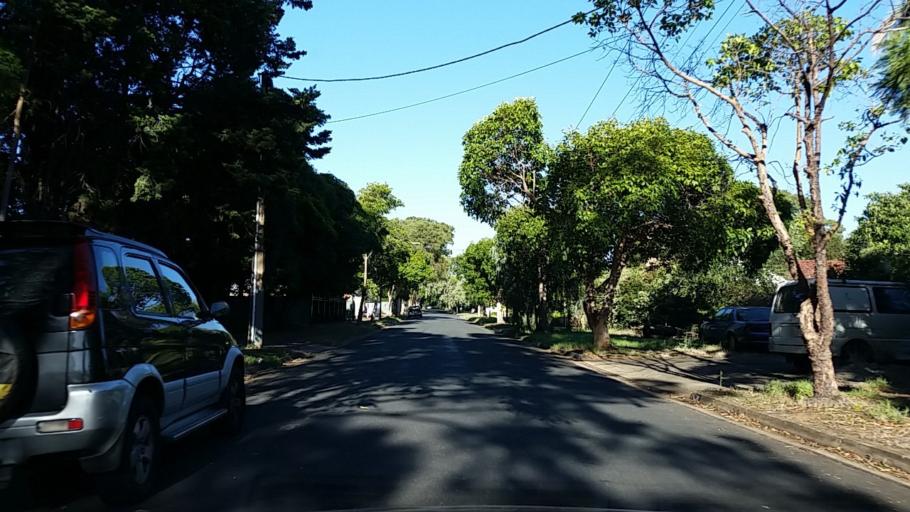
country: AU
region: South Australia
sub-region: Salisbury
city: Salisbury
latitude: -34.7607
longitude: 138.6378
